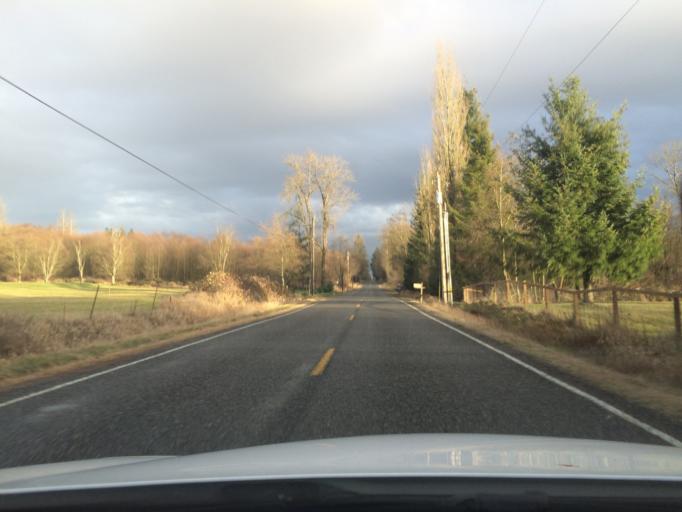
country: CA
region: British Columbia
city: Langley
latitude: 48.9934
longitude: -122.5813
